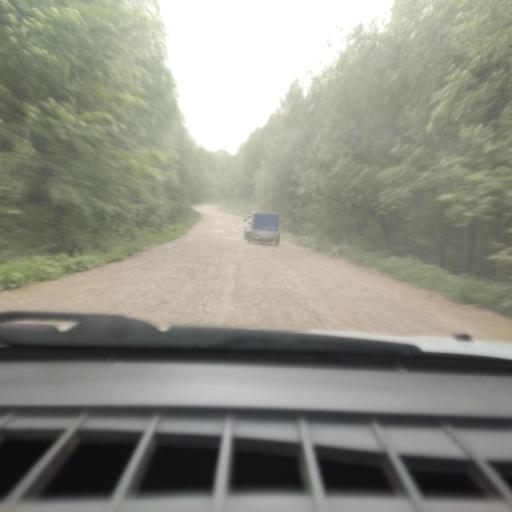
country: RU
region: Perm
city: Novyye Lyady
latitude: 57.8987
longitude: 56.6551
